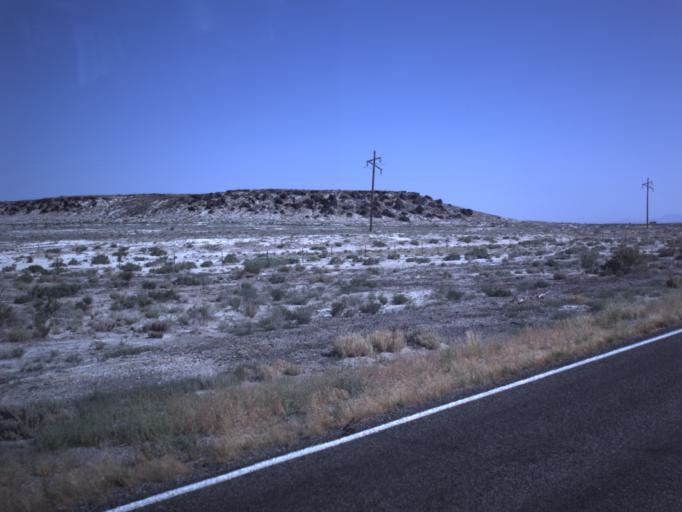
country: US
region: Utah
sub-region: Millard County
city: Delta
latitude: 39.1789
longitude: -112.7012
